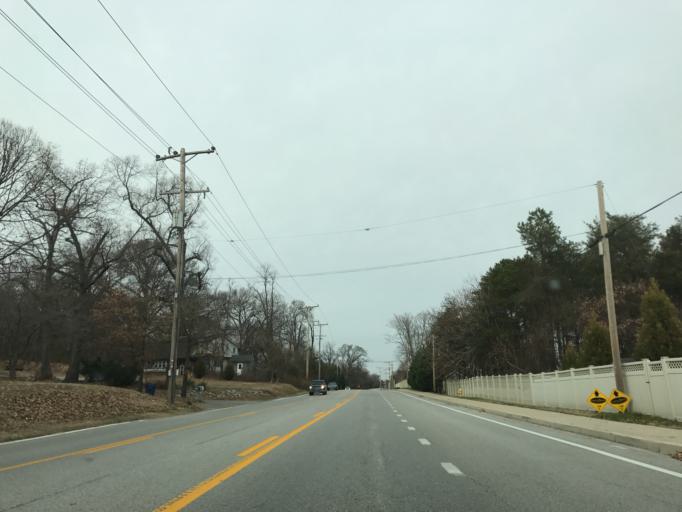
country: US
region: Maryland
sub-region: Anne Arundel County
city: Pasadena
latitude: 39.1249
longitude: -76.5622
